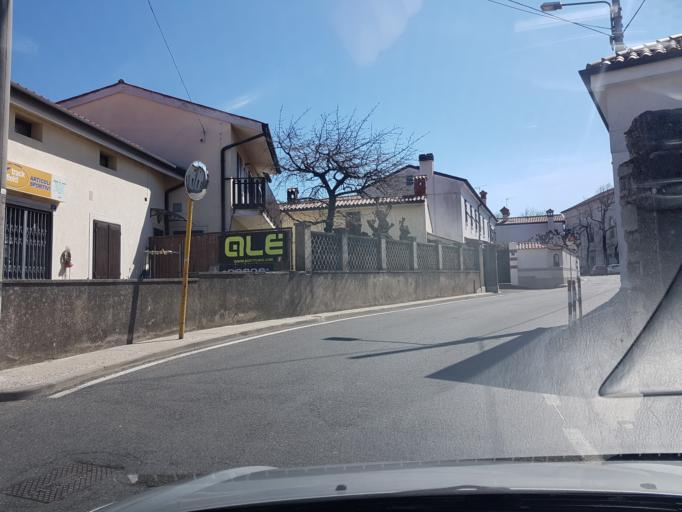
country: IT
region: Friuli Venezia Giulia
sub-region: Provincia di Trieste
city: Dolina
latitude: 45.6429
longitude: 13.8633
